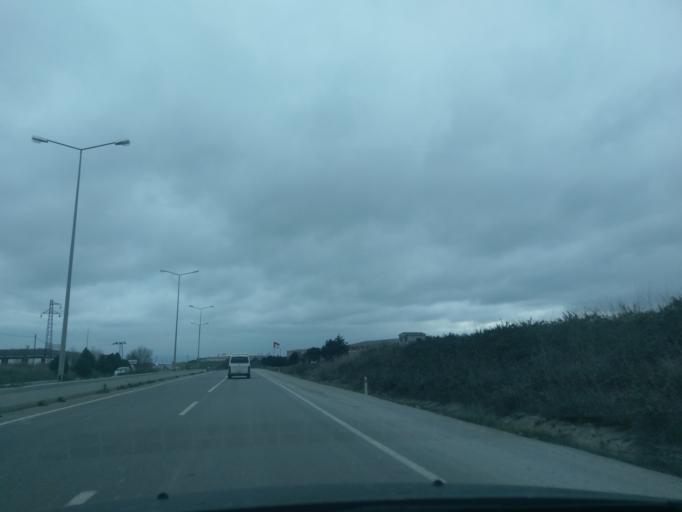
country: TR
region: Istanbul
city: Muratbey
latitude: 41.1171
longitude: 28.4967
